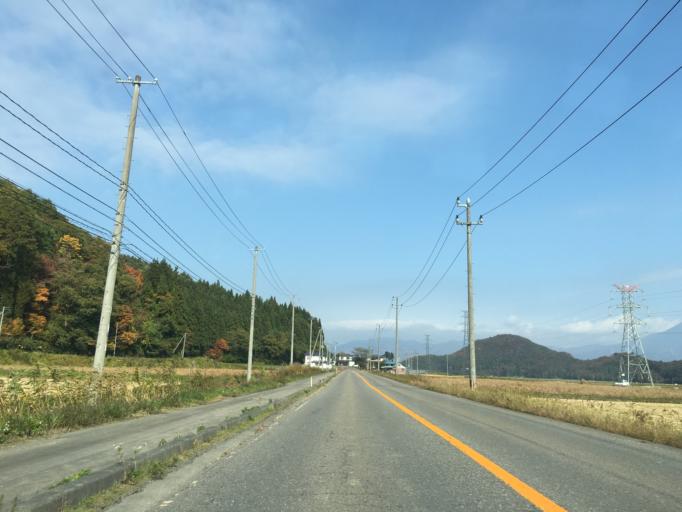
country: JP
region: Fukushima
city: Inawashiro
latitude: 37.4828
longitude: 140.0100
